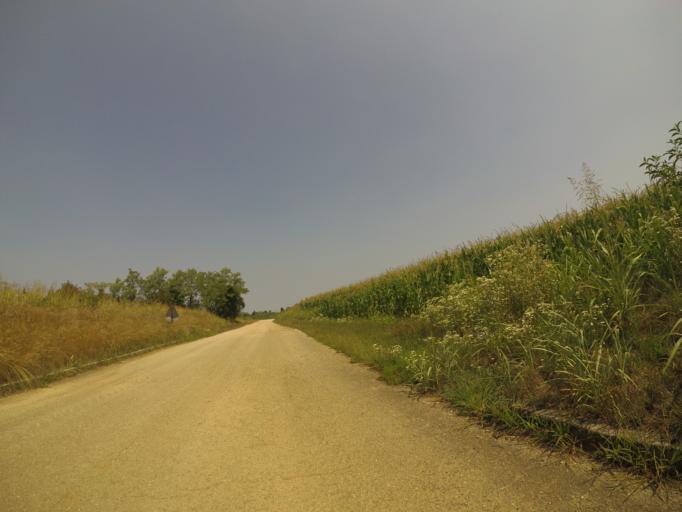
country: IT
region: Friuli Venezia Giulia
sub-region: Provincia di Udine
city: Basiliano-Vissandone
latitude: 46.0080
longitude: 13.0938
